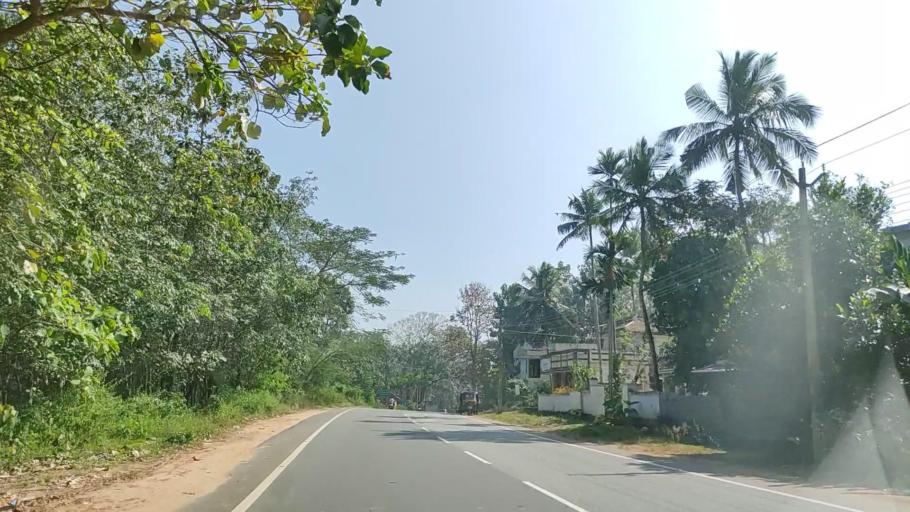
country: IN
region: Kerala
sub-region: Kollam
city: Punalur
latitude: 8.9300
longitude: 76.9870
